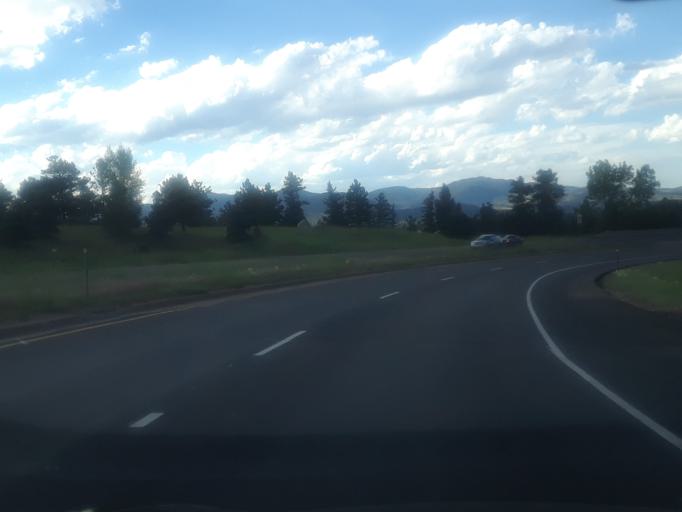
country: US
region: Colorado
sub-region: Jefferson County
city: Kittredge
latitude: 39.6961
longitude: -105.3389
